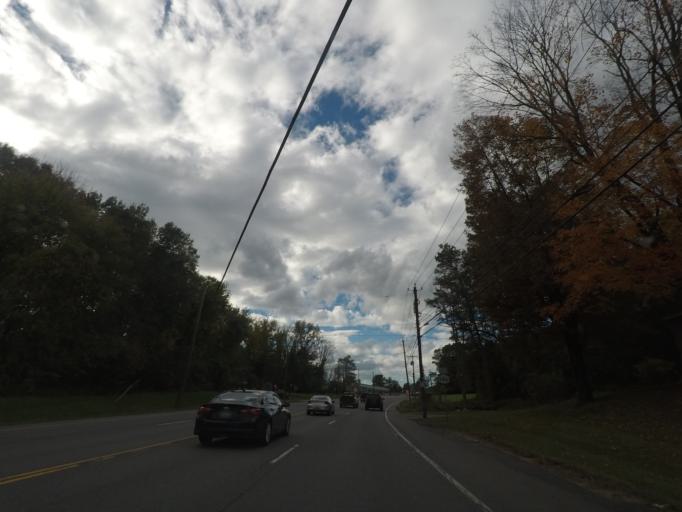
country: US
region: New York
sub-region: Albany County
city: Westmere
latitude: 42.7066
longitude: -73.9191
